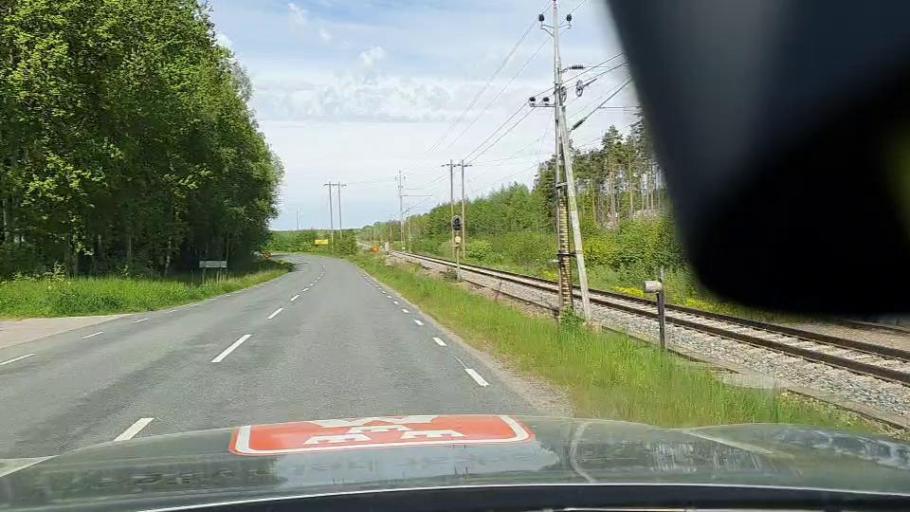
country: SE
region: Soedermanland
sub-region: Eskilstuna Kommun
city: Skogstorp
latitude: 59.3001
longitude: 16.4605
